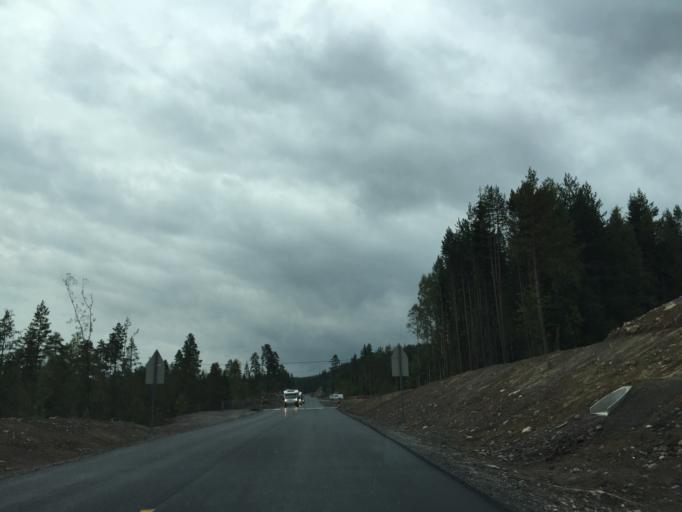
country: NO
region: Hedmark
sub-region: Loten
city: Loten
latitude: 60.6516
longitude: 11.3894
